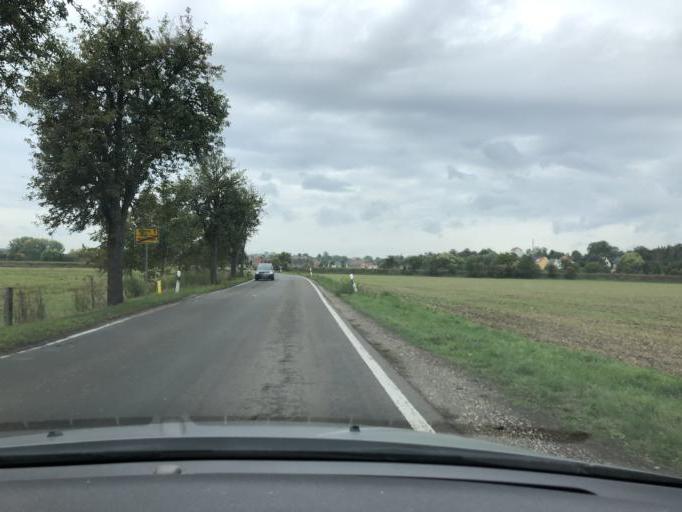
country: DE
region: Saxony-Anhalt
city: Uichteritz
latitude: 51.2112
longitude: 11.9339
